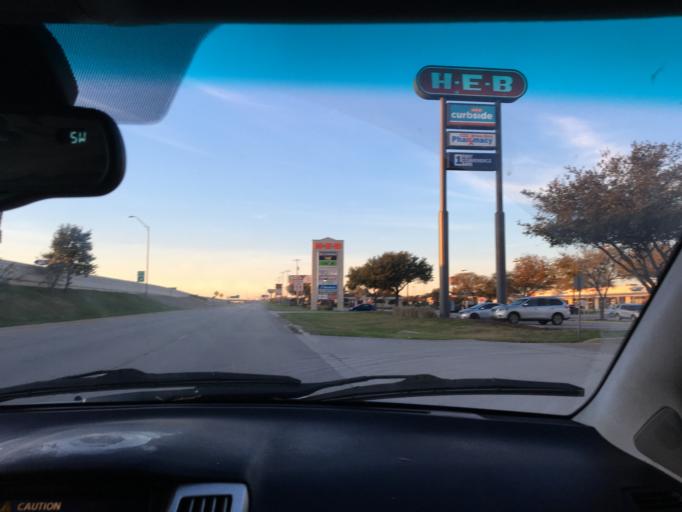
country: US
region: Texas
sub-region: Hays County
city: Buda
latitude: 30.0879
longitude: -97.8199
